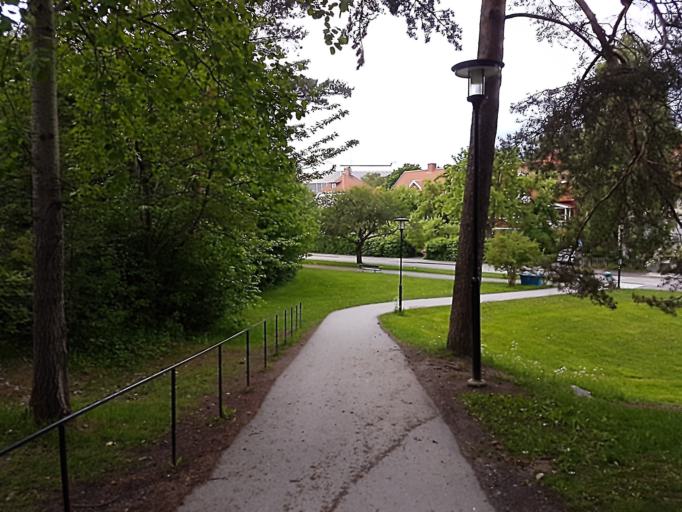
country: SE
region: Stockholm
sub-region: Stockholms Kommun
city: Arsta
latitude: 59.2855
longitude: 18.0853
